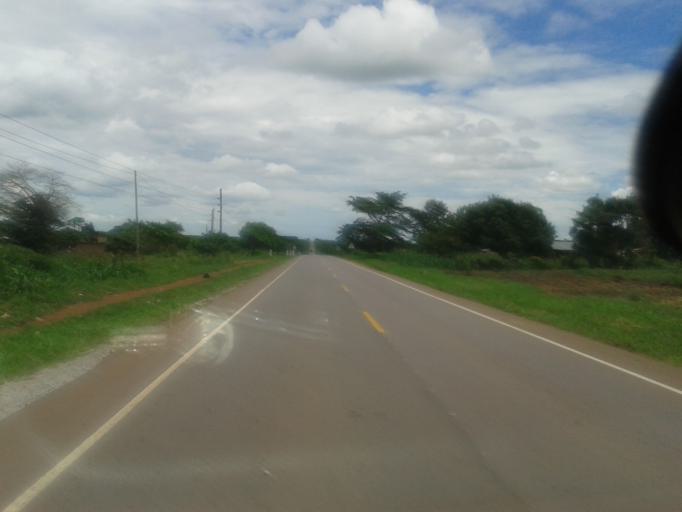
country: UG
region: Western Region
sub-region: Kiryandongo District
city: Masindi Port
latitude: 1.7650
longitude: 32.0200
